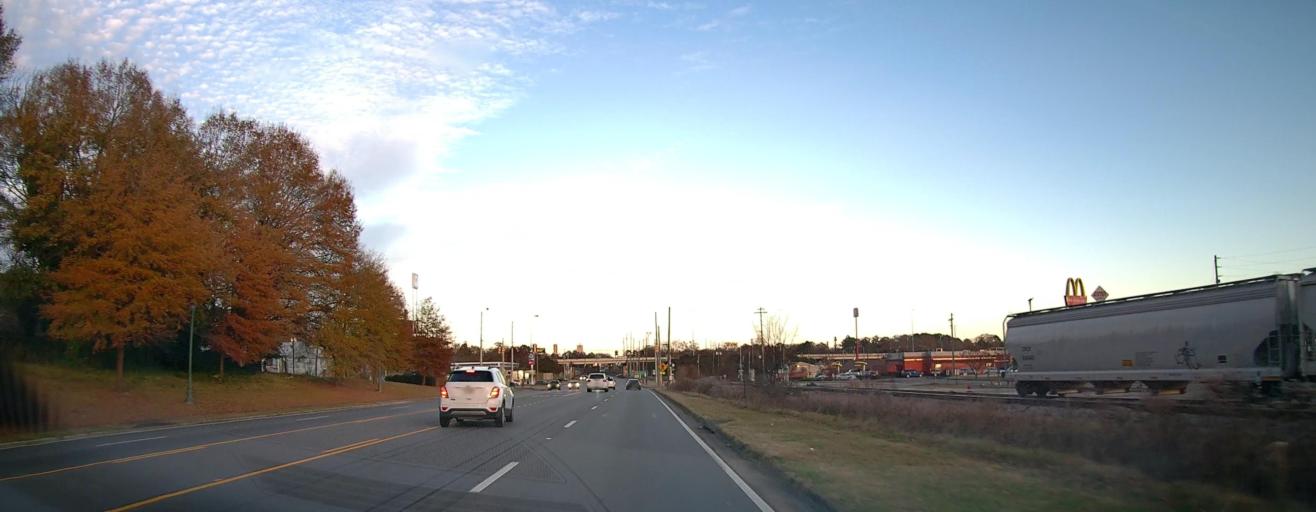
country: US
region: Alabama
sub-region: Etowah County
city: Attalla
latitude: 34.0190
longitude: -86.0786
